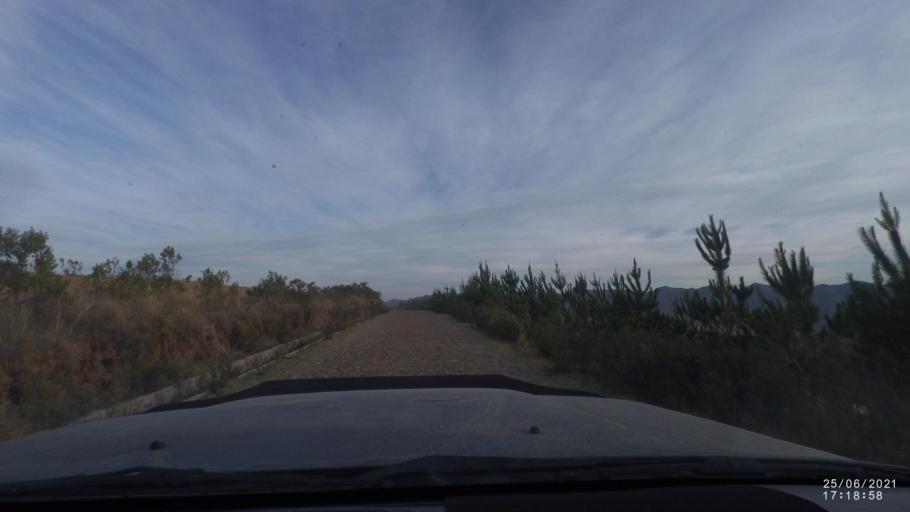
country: BO
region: Cochabamba
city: Arani
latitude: -17.8978
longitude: -65.6925
